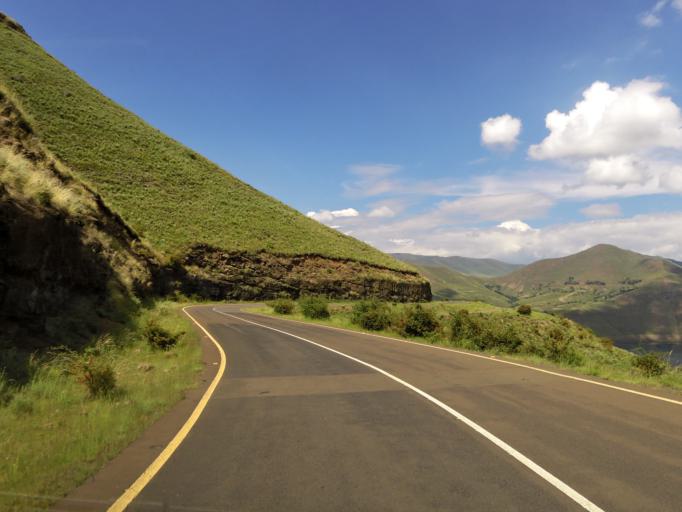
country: LS
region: Thaba-Tseka
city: Thaba-Tseka
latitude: -29.1515
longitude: 28.4806
